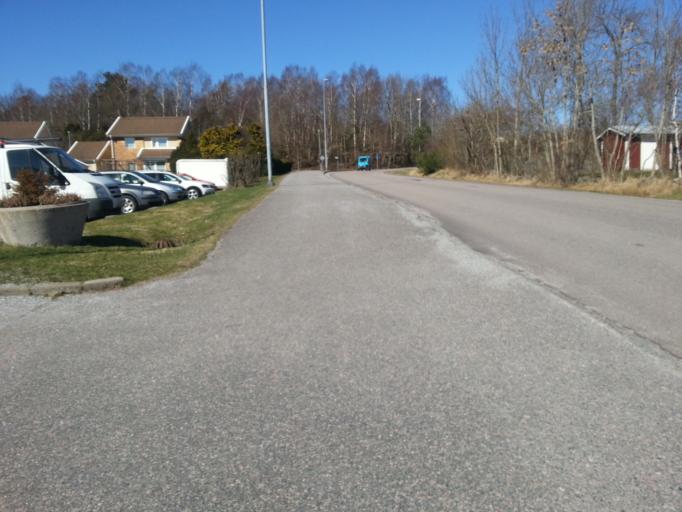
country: SE
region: Vaestra Goetaland
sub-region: Kungalvs Kommun
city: Kungalv
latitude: 57.8912
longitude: 11.9702
